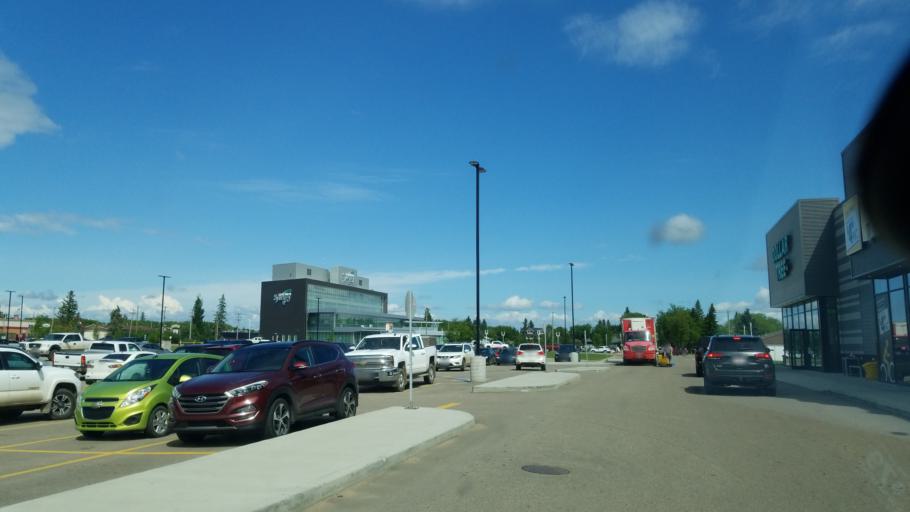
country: CA
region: Saskatchewan
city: Lloydminster
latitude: 53.2761
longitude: -110.0079
